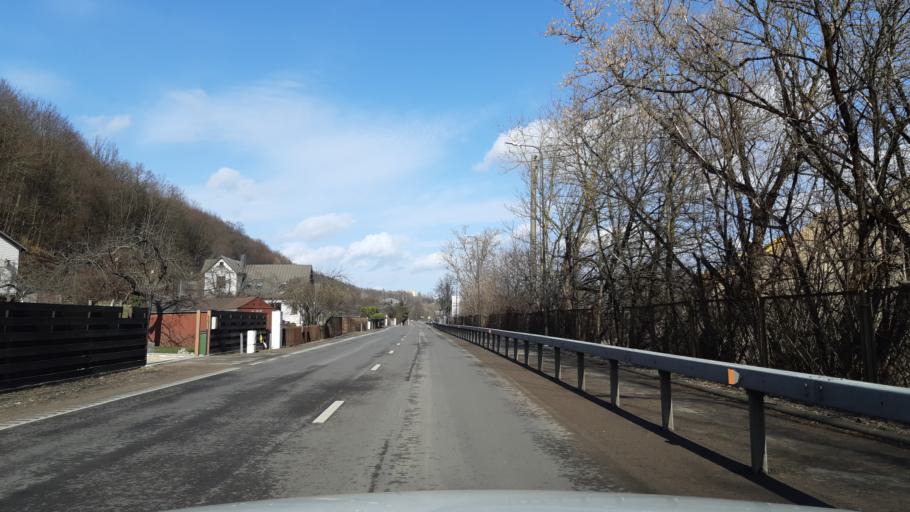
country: LT
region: Kauno apskritis
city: Dainava (Kaunas)
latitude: 54.8777
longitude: 23.9576
